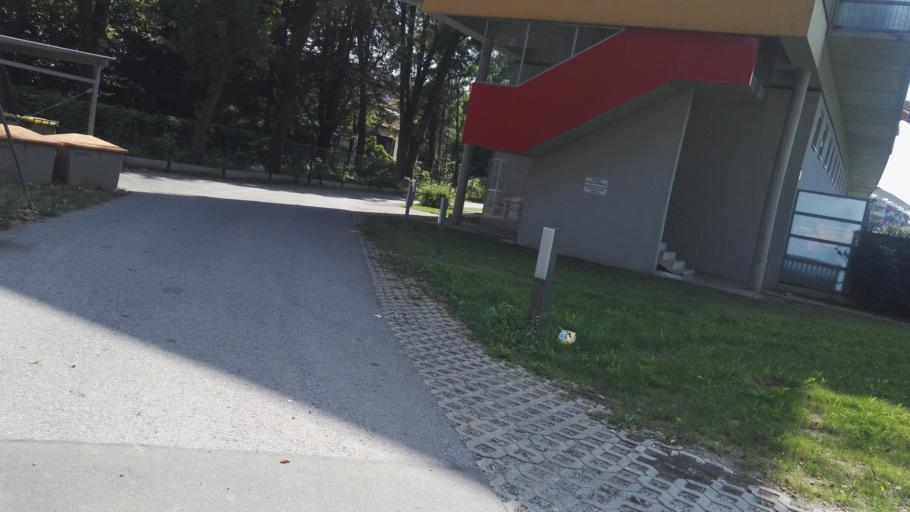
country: AT
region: Styria
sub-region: Graz Stadt
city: Goesting
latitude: 47.0888
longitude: 15.4146
